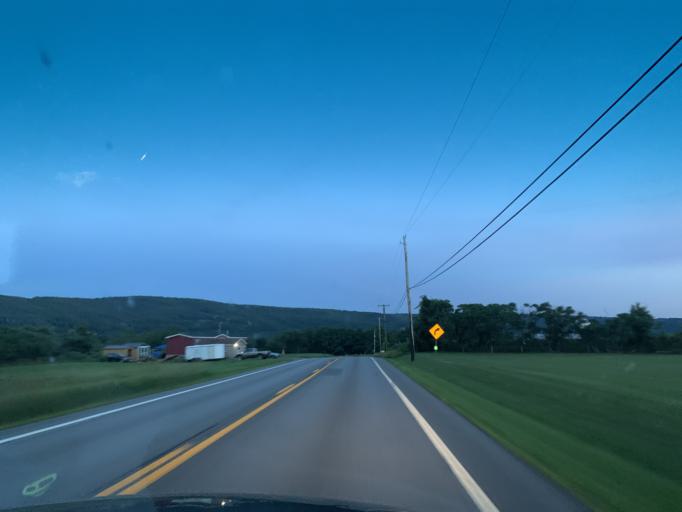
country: US
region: New York
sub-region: Chenango County
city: New Berlin
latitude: 42.5893
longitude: -75.3359
